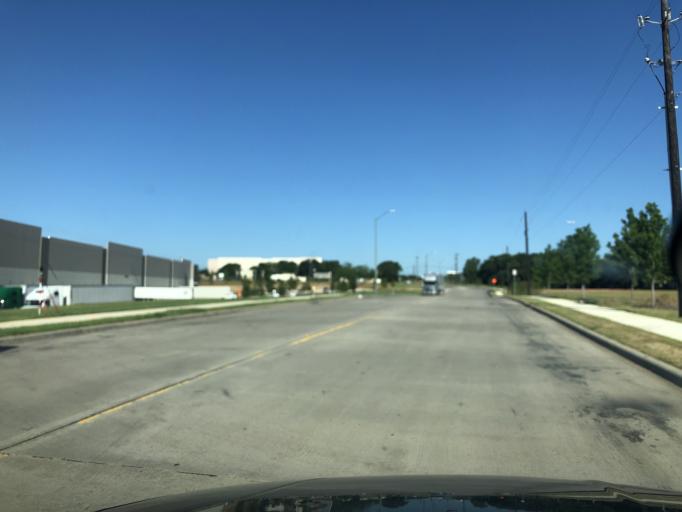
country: US
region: Texas
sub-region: Tarrant County
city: Euless
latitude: 32.8216
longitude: -97.0273
